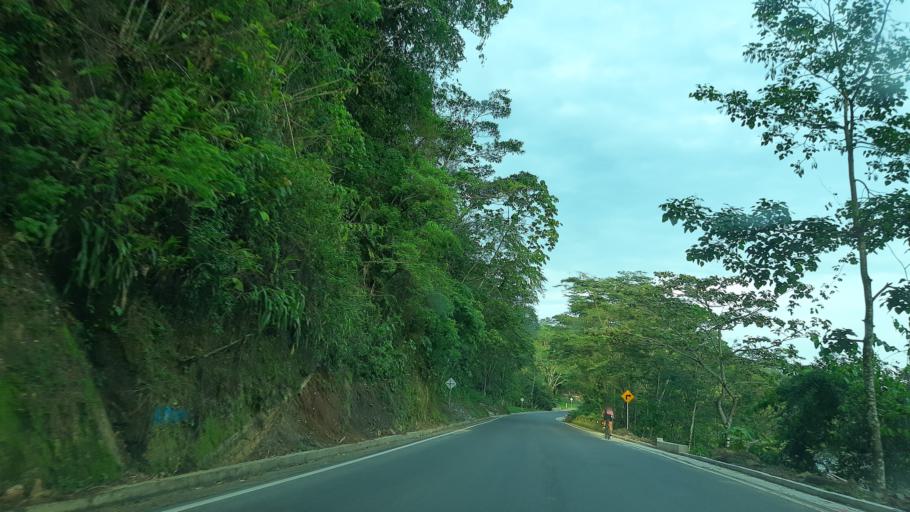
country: CO
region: Boyaca
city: San Luis de Gaceno
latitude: 4.8276
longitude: -73.1074
